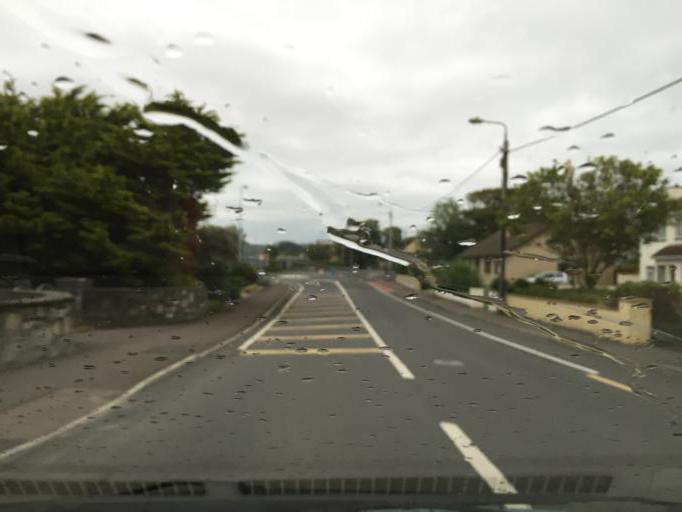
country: IE
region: Connaught
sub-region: Sligo
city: Strandhill
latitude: 54.2694
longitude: -8.5932
